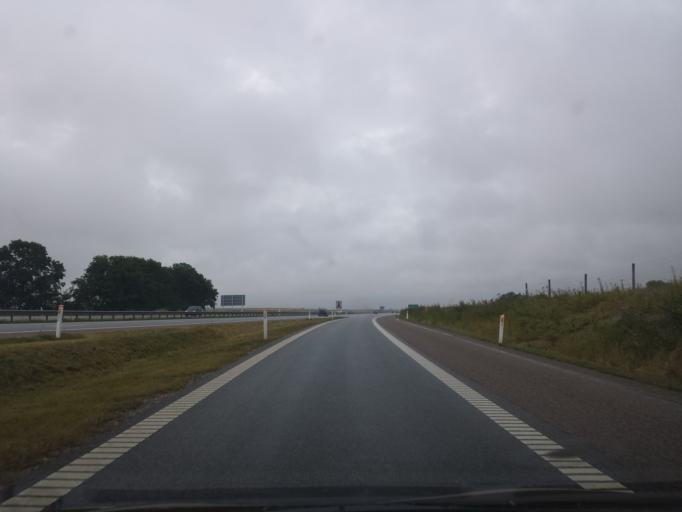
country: DK
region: South Denmark
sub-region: Sonderborg Kommune
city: Grasten
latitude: 54.9499
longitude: 9.6417
